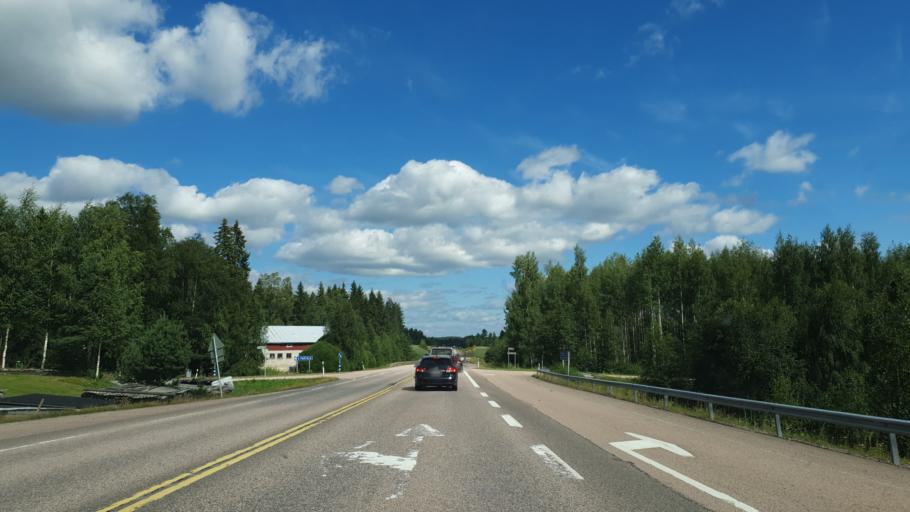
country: FI
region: Central Finland
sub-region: Jaemsae
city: Jaemsae
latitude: 61.8336
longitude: 25.0979
